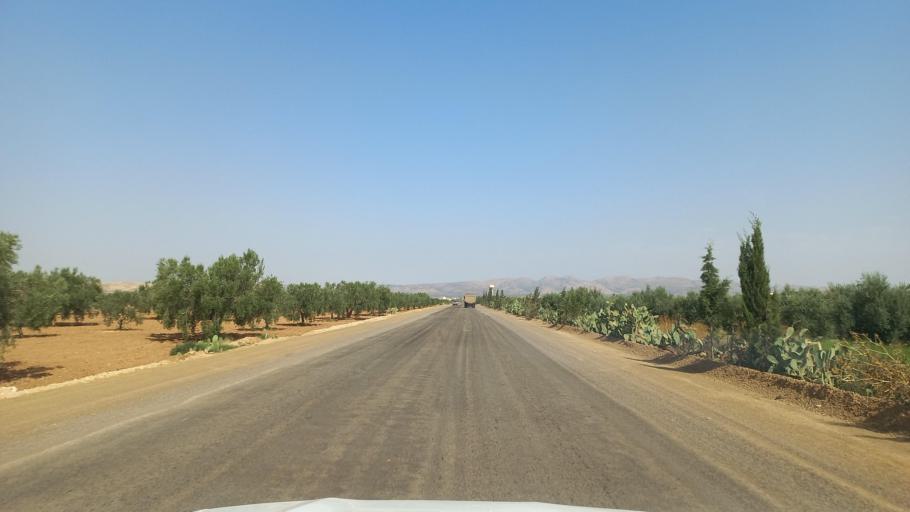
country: TN
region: Al Qasrayn
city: Sbiba
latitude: 35.3490
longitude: 9.0527
